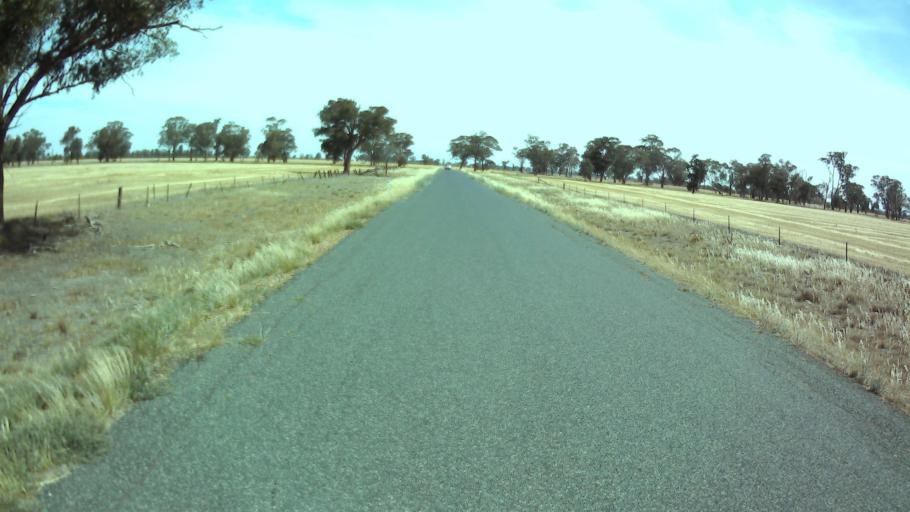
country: AU
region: New South Wales
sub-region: Weddin
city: Grenfell
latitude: -34.0028
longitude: 147.7738
